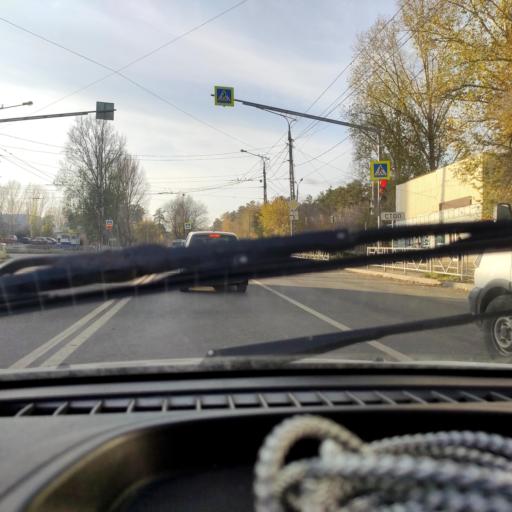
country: RU
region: Samara
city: Zhigulevsk
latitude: 53.4829
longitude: 49.4612
